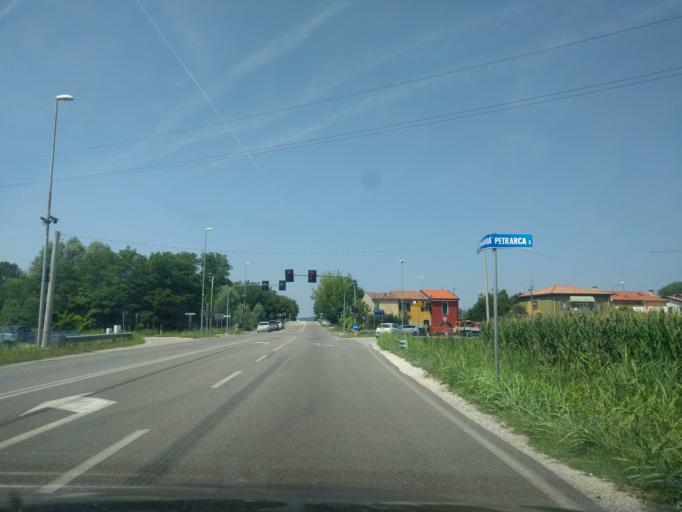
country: IT
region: Veneto
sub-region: Provincia di Padova
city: Monselice
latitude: 45.2465
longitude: 11.7588
